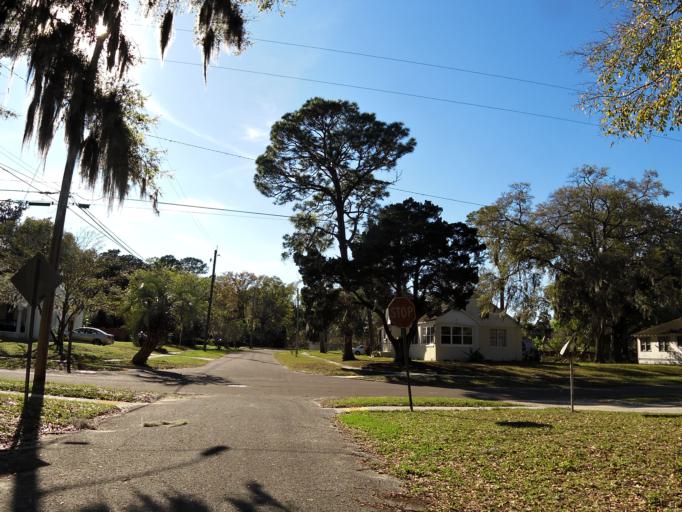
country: US
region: Florida
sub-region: Duval County
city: Jacksonville
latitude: 30.3816
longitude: -81.6468
